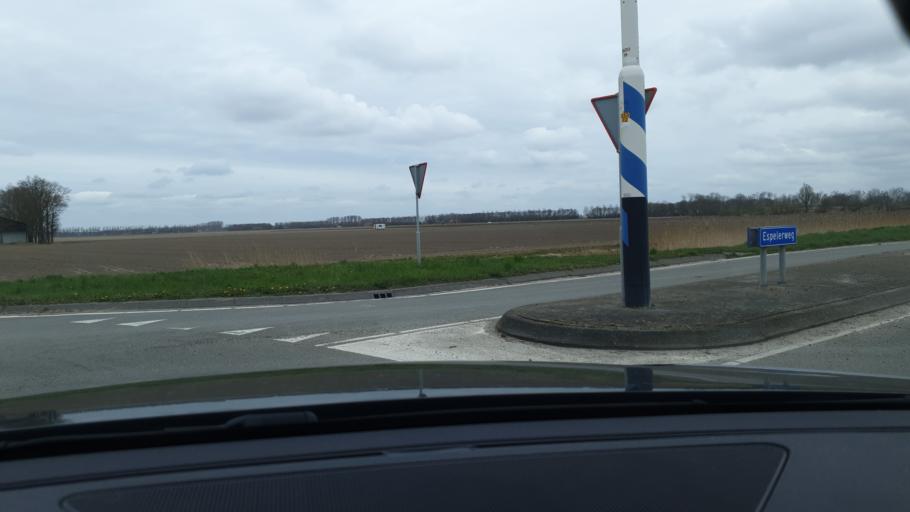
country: NL
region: Flevoland
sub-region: Gemeente Urk
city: Urk
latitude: 52.7247
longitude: 5.6462
